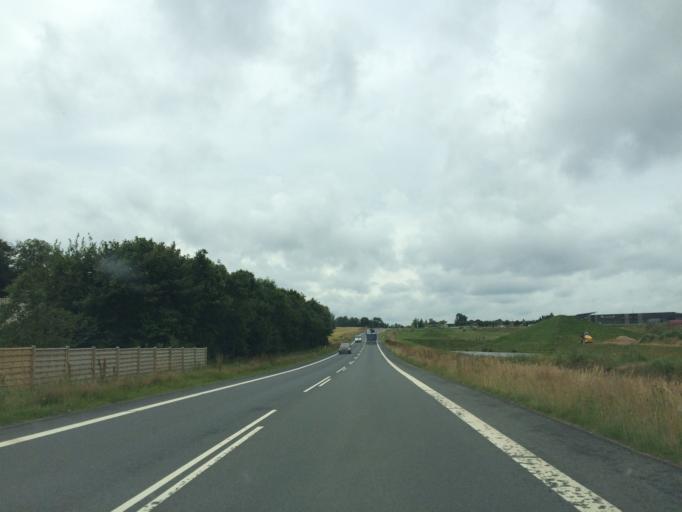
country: DK
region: Central Jutland
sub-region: Silkeborg Kommune
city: Silkeborg
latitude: 56.2062
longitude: 9.6032
